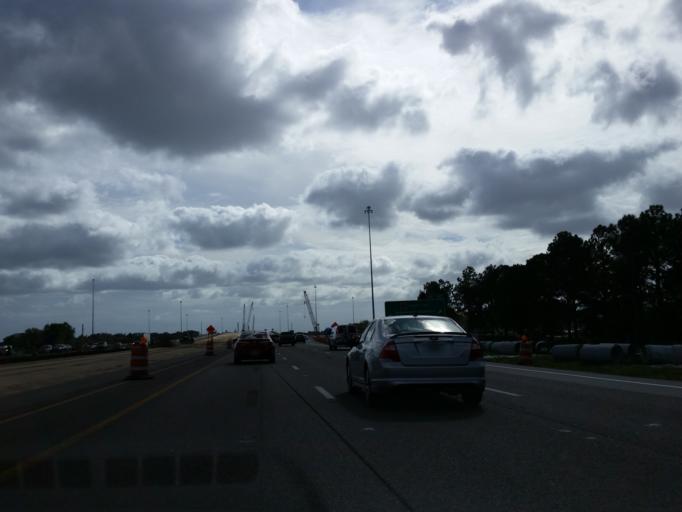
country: US
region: Florida
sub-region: Sarasota County
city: The Meadows
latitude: 27.3951
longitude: -82.4508
